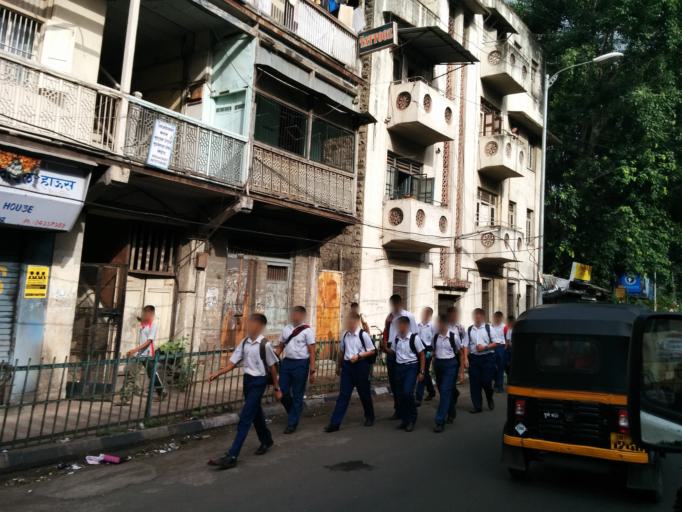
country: IN
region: Maharashtra
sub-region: Pune Division
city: Pune
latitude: 18.5108
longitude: 73.8457
